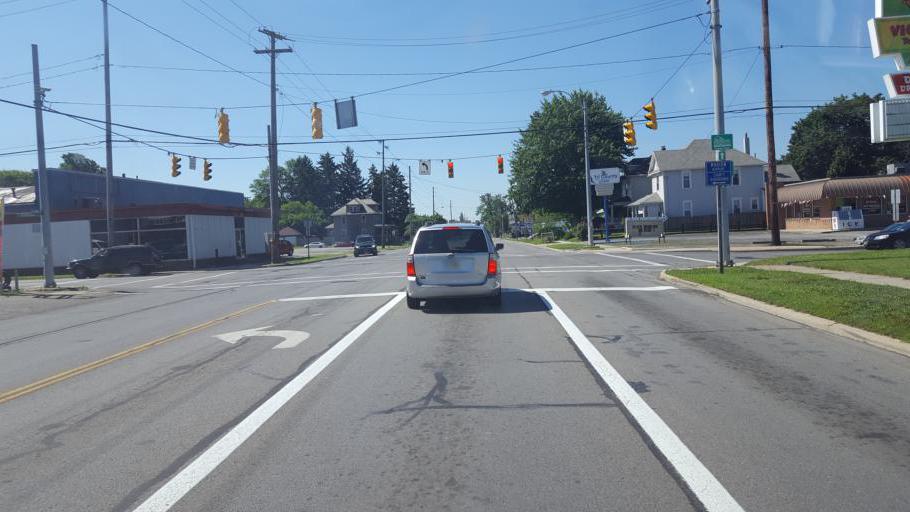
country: US
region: Ohio
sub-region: Marion County
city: Marion
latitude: 40.6006
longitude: -83.1297
